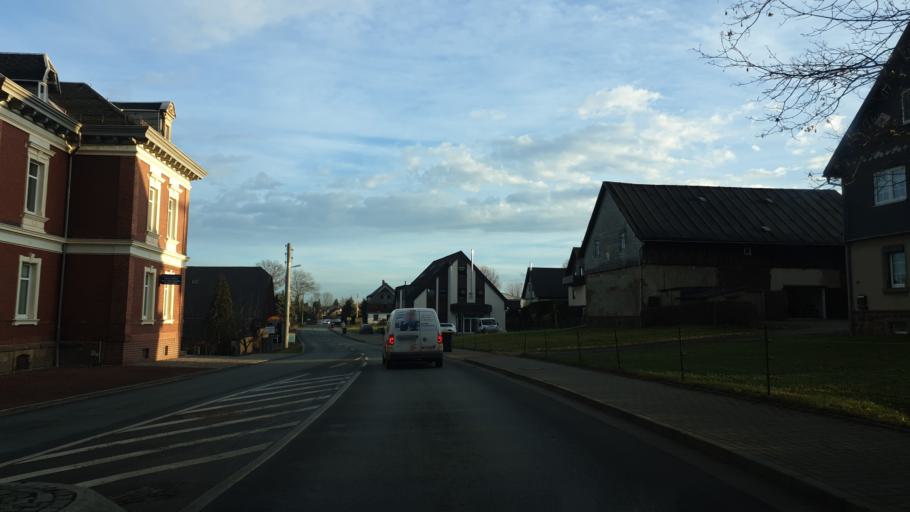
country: DE
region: Saxony
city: Neukirchen
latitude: 50.8006
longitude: 12.8028
